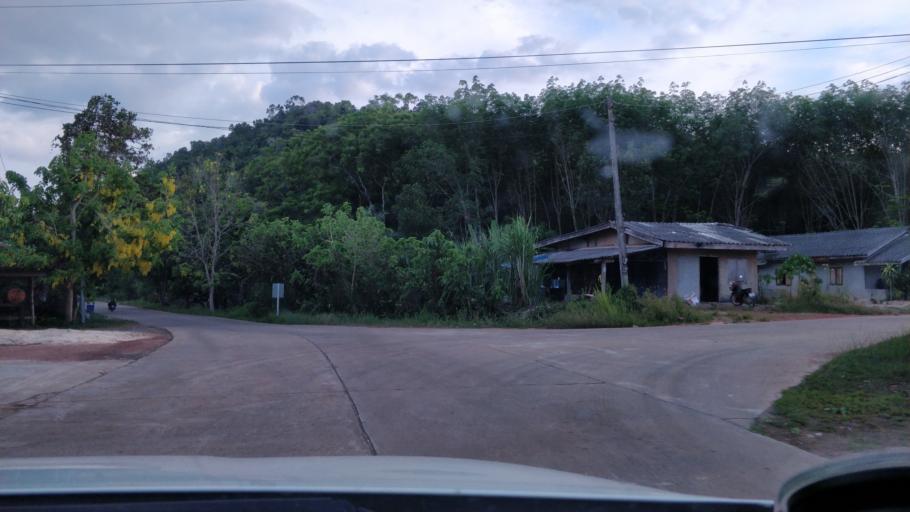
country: TH
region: Krabi
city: Saladan
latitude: 7.5822
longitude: 99.0674
